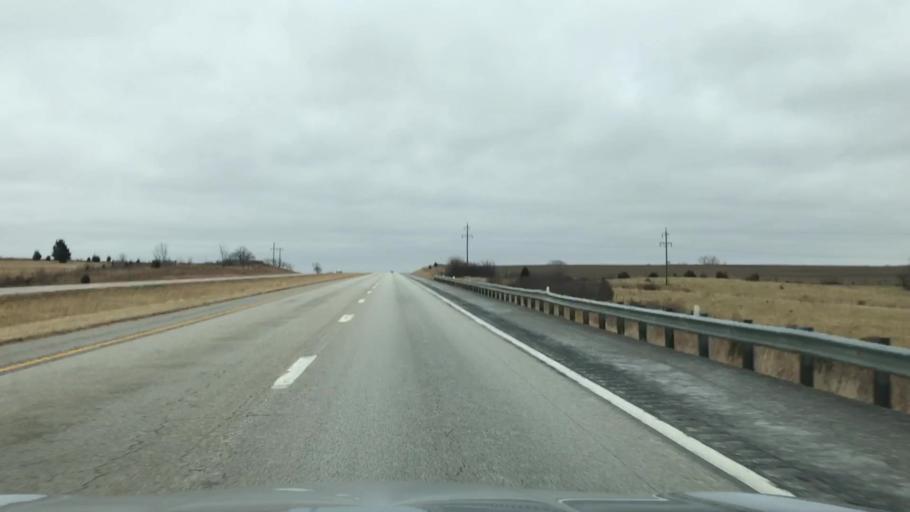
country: US
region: Missouri
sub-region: Caldwell County
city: Hamilton
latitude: 39.7496
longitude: -94.0892
